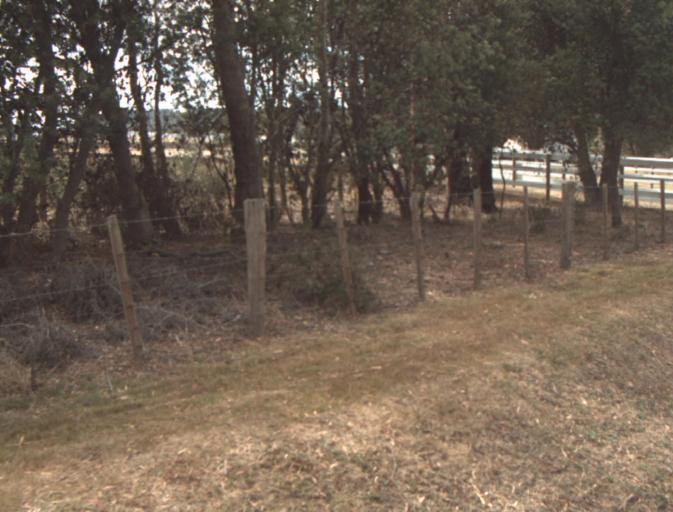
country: AU
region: Tasmania
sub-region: Launceston
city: Mayfield
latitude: -41.2801
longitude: 147.0437
